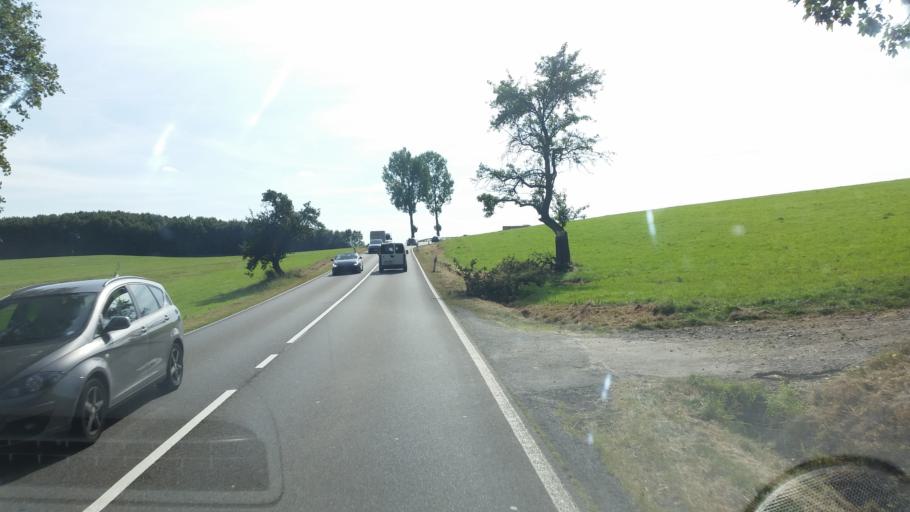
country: DE
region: Rheinland-Pfalz
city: Kaden
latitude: 50.5525
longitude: 7.8896
